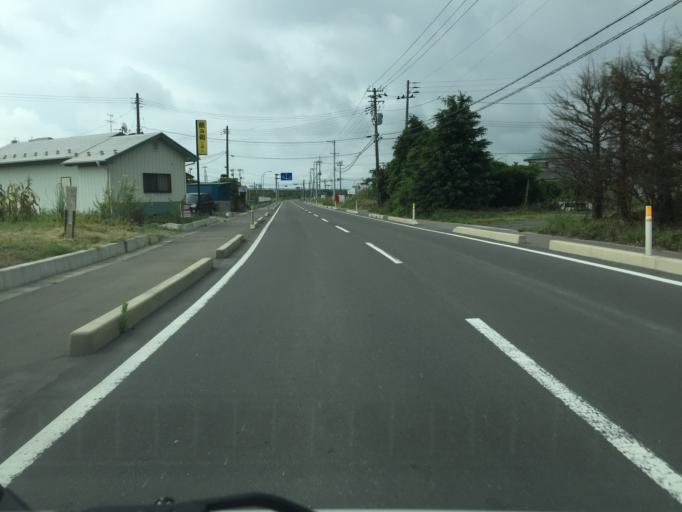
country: JP
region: Miyagi
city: Watari
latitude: 38.0327
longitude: 140.8889
